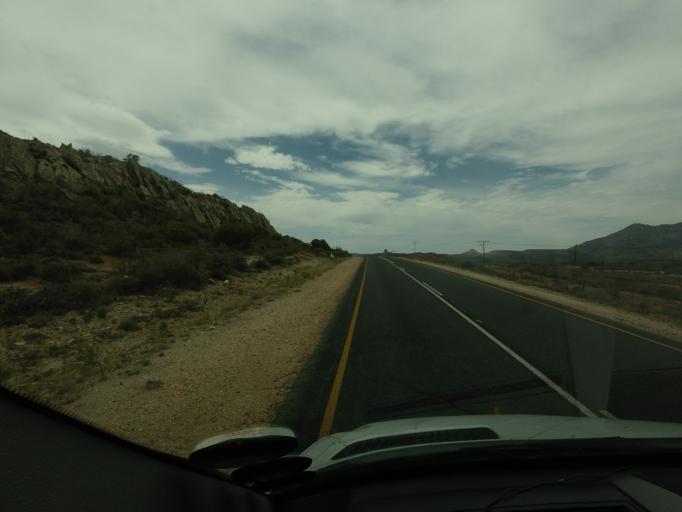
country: ZA
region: Western Cape
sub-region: Overberg District Municipality
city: Swellendam
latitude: -33.8519
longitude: 20.8259
